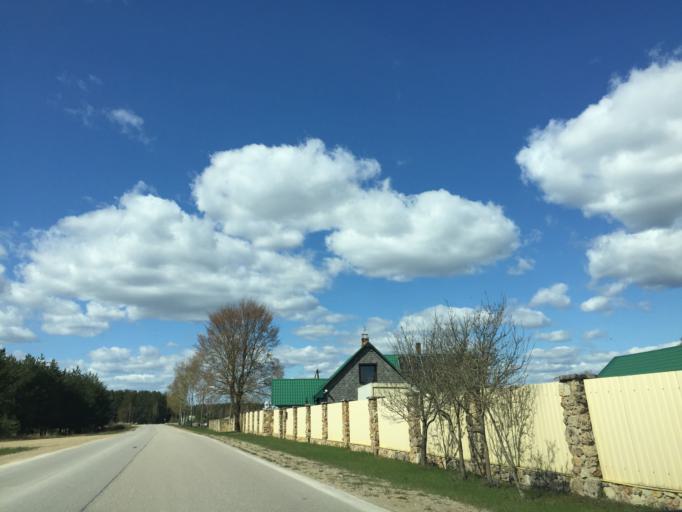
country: LV
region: Vilanu
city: Vilani
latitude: 56.5712
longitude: 27.0469
